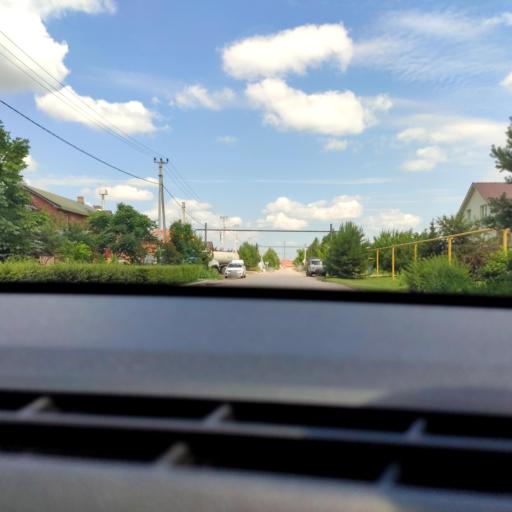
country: RU
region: Samara
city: Podstepki
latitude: 53.5695
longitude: 49.0795
